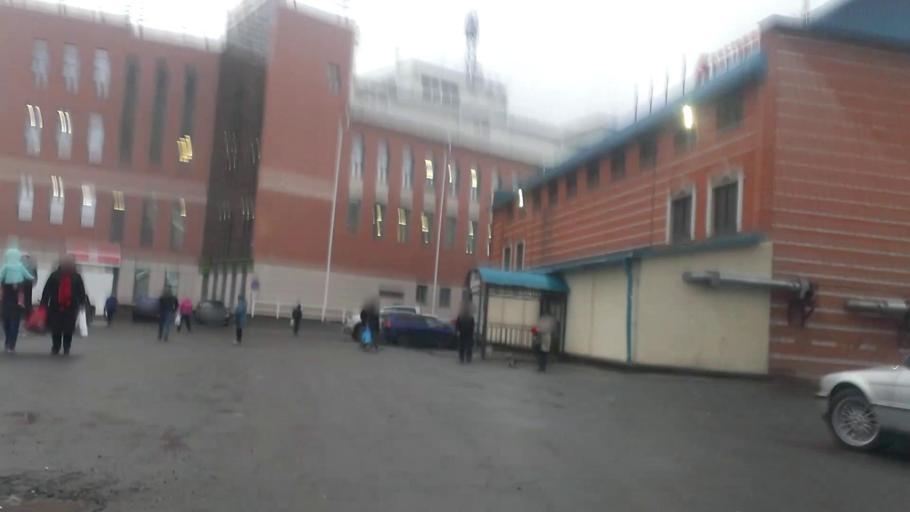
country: RU
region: Altai Krai
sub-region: Gorod Barnaulskiy
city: Barnaul
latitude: 53.3582
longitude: 83.6981
